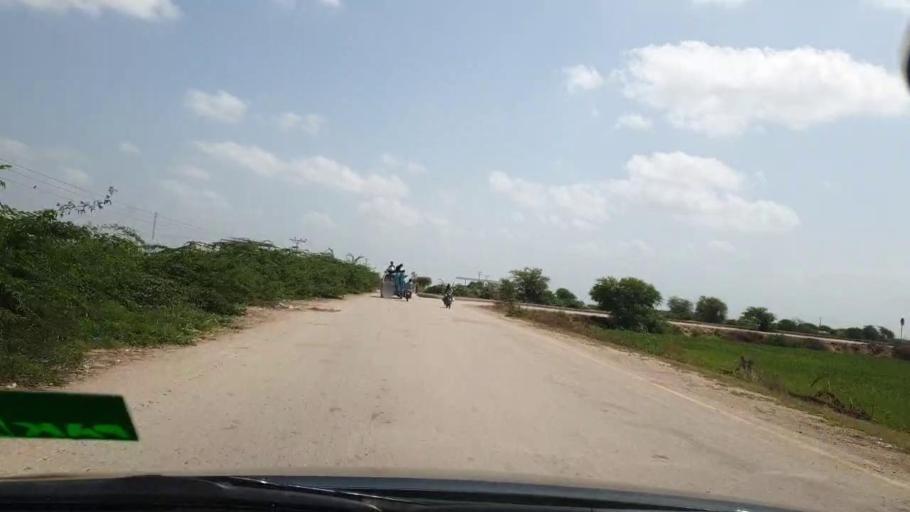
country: PK
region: Sindh
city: Kadhan
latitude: 24.6275
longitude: 69.1883
